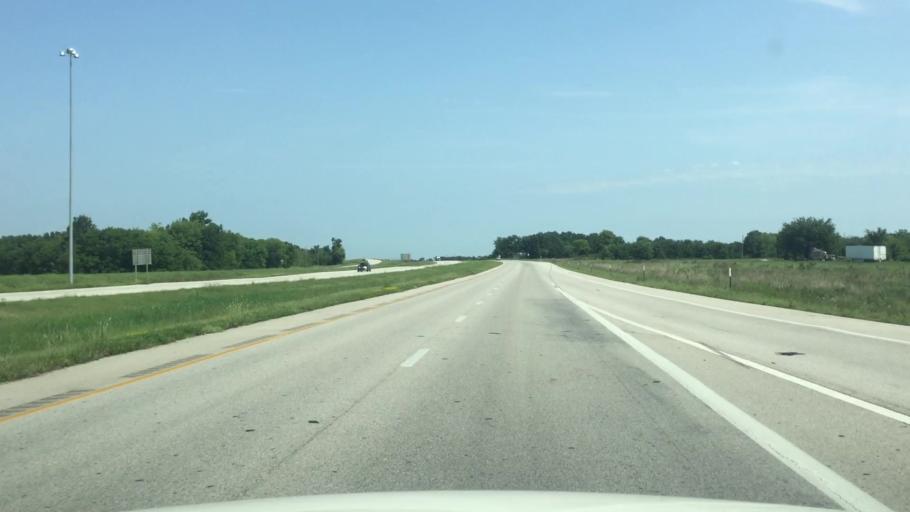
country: US
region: Kansas
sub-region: Montgomery County
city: Coffeyville
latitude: 37.0498
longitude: -95.5805
